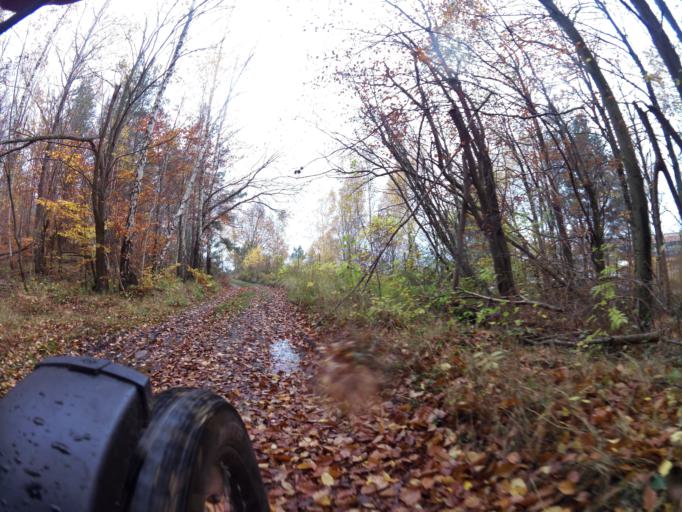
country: PL
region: Pomeranian Voivodeship
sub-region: Powiat wejherowski
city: Gniewino
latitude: 54.7540
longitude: 18.0841
